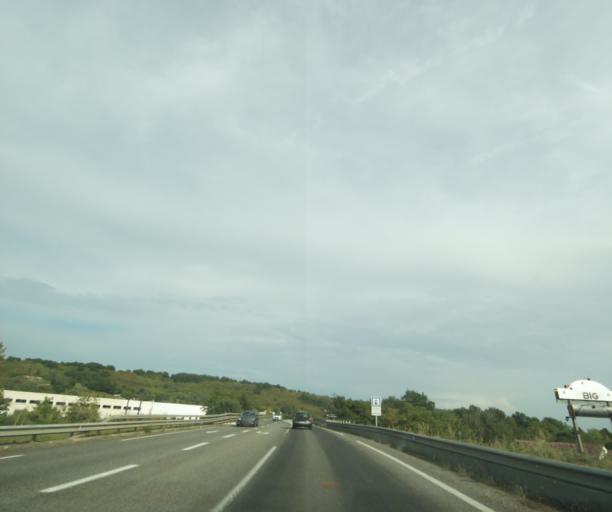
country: FR
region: Midi-Pyrenees
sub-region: Departement du Tarn-et-Garonne
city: Grisolles
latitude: 43.8364
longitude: 1.2944
